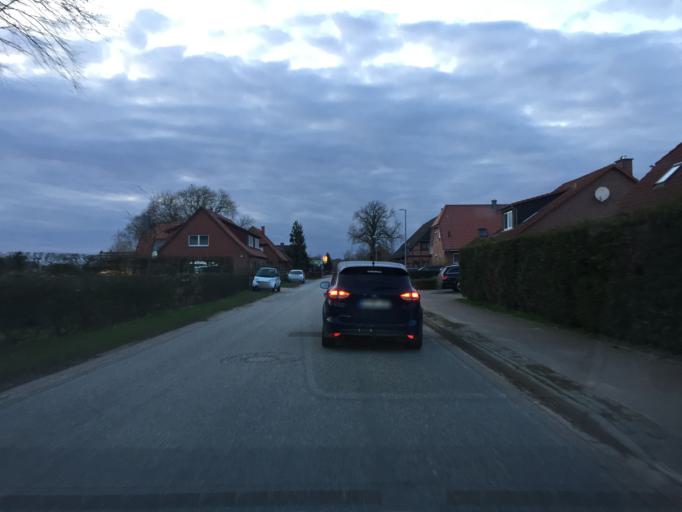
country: DE
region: Lower Saxony
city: Neustadt am Rubenberge
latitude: 52.5753
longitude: 9.4201
